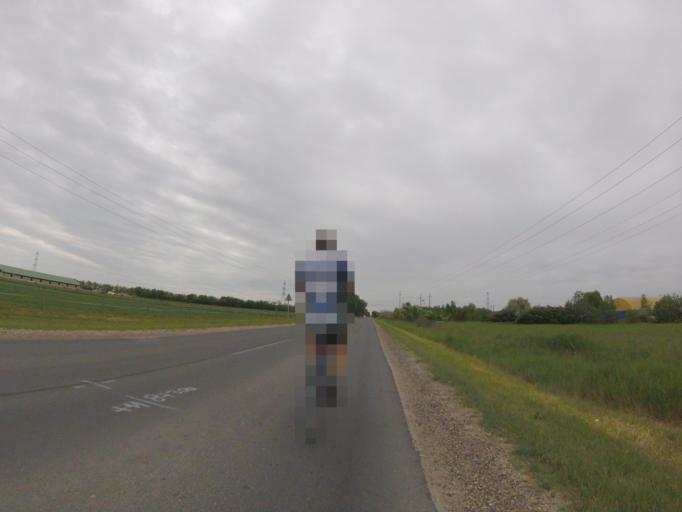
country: HU
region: Pest
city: Bugyi
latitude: 47.2349
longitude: 19.1851
